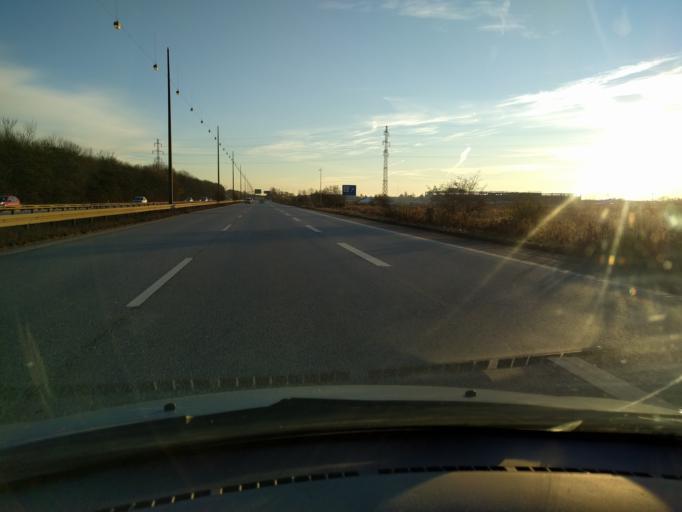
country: DK
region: Capital Region
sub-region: Ishoj Kommune
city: Ishoj
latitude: 55.6293
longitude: 12.3297
